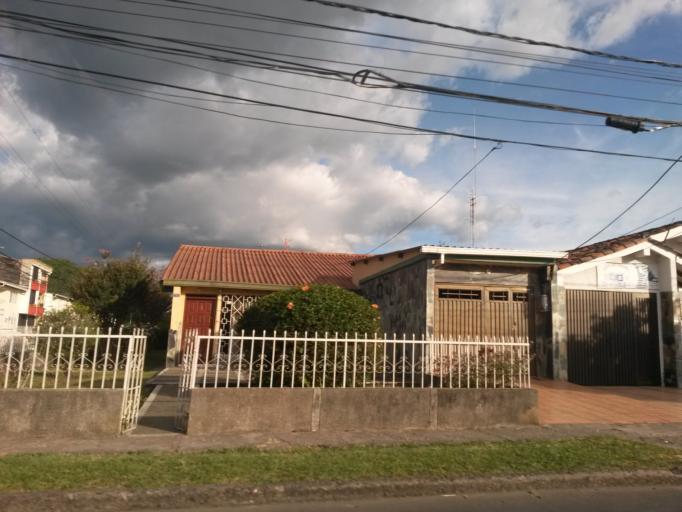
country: CO
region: Cauca
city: Popayan
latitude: 2.4537
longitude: -76.6045
